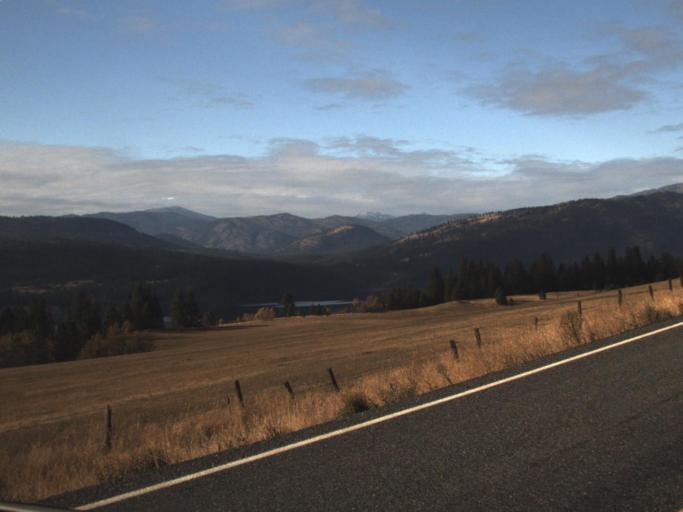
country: US
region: Washington
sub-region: Stevens County
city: Kettle Falls
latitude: 48.4052
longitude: -118.1702
